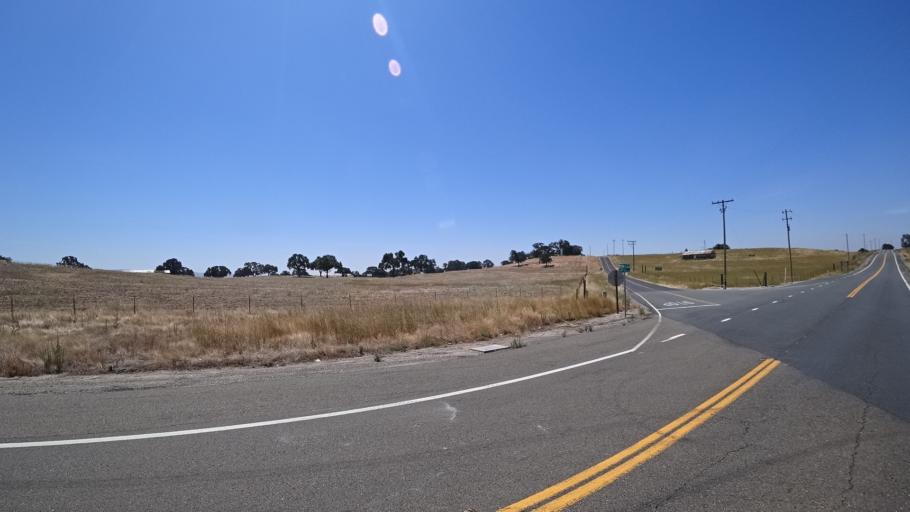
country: US
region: California
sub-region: Calaveras County
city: Rancho Calaveras
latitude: 38.0945
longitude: -120.9448
